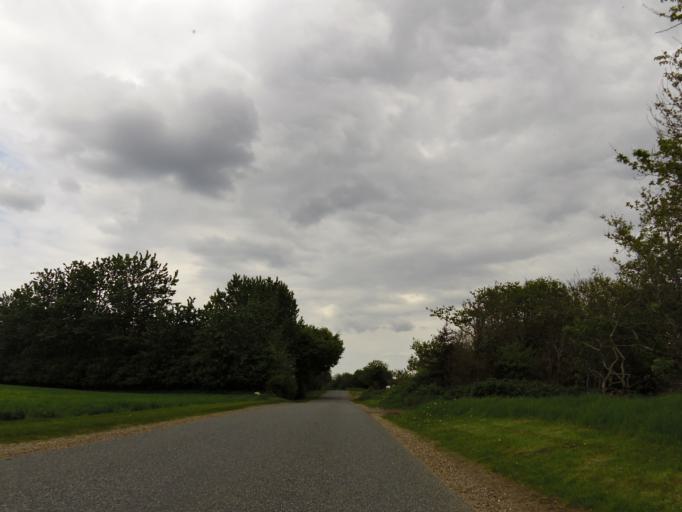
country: DK
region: Central Jutland
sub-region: Holstebro Kommune
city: Vinderup
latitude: 56.5313
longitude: 8.8021
